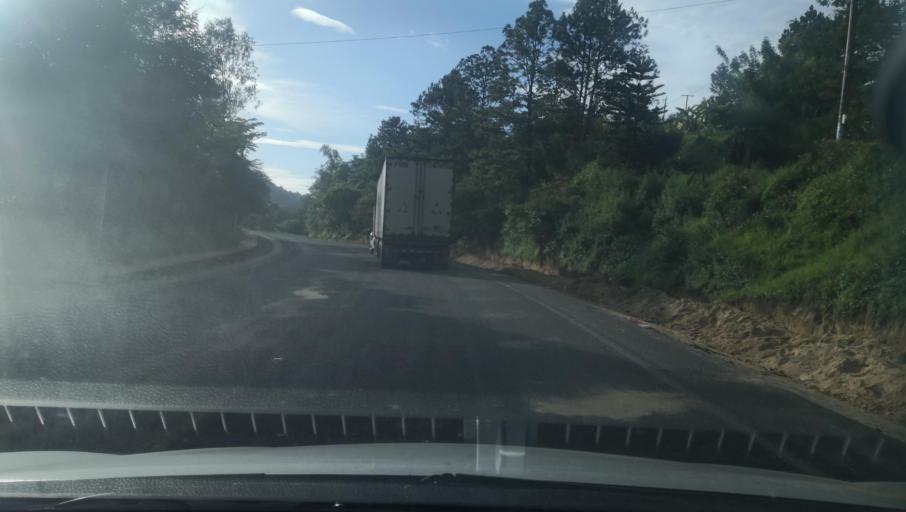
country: NI
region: Nueva Segovia
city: Mozonte
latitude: 13.7304
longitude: -86.5105
